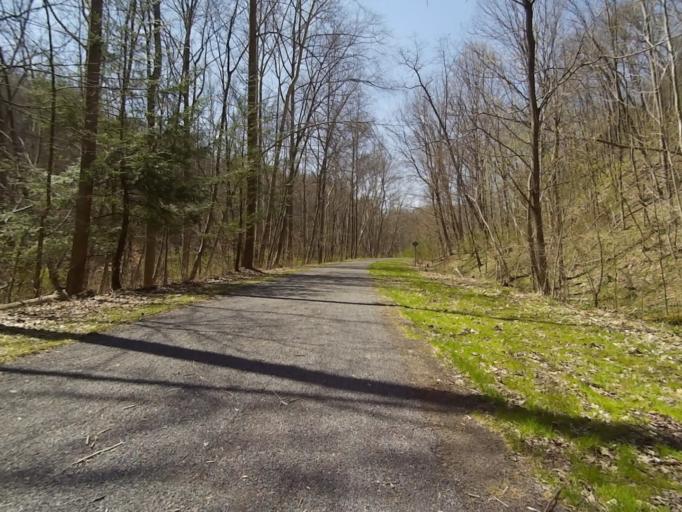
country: US
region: Pennsylvania
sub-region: Blair County
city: Williamsburg
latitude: 40.5485
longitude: -78.1459
